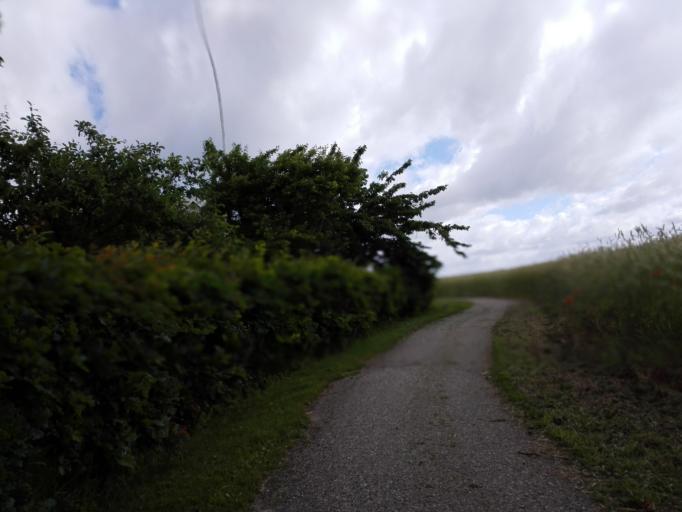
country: DK
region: Capital Region
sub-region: Egedal Kommune
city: Olstykke
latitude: 55.8080
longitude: 12.1433
